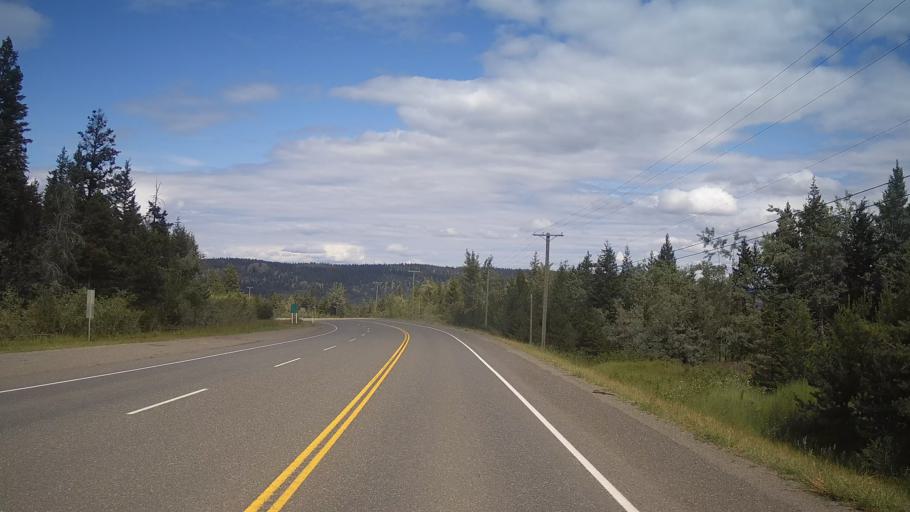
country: CA
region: British Columbia
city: Cache Creek
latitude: 51.6050
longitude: -121.2900
